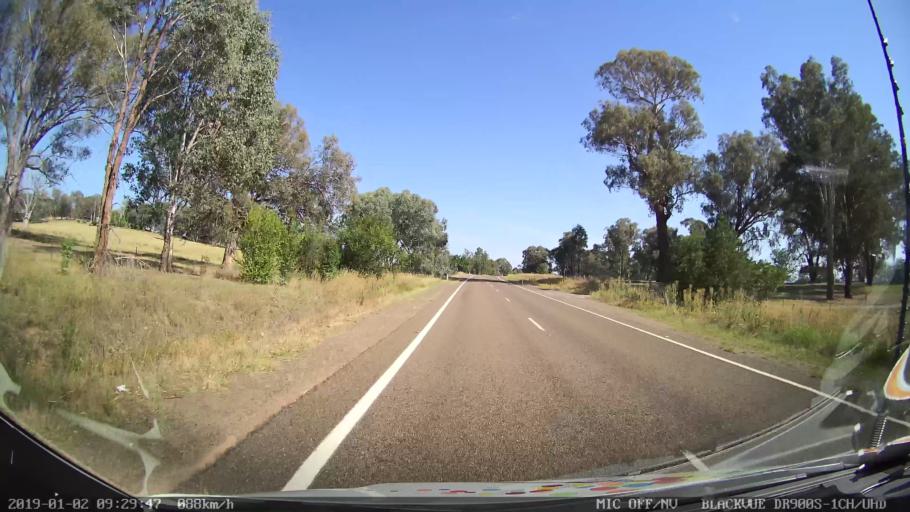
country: AU
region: New South Wales
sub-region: Tumut Shire
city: Tumut
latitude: -35.3349
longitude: 148.2396
